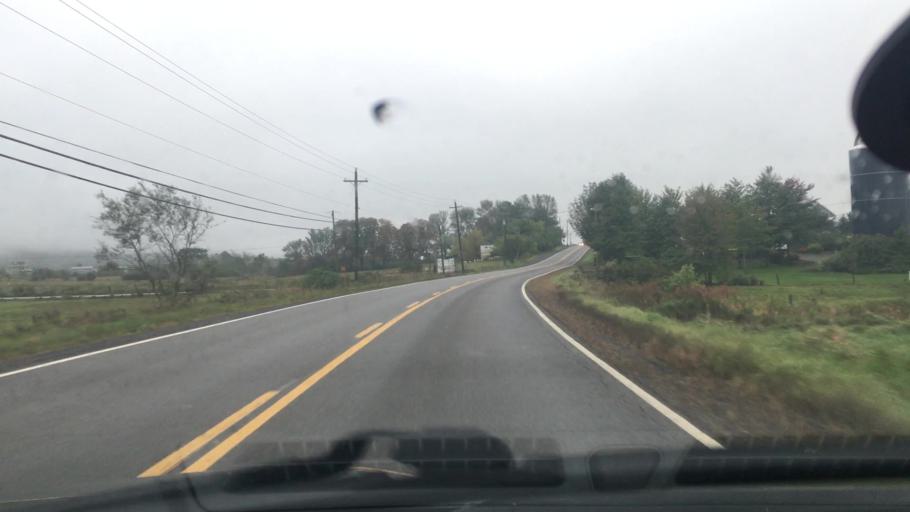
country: CA
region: Nova Scotia
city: Windsor
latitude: 44.9701
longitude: -64.1406
